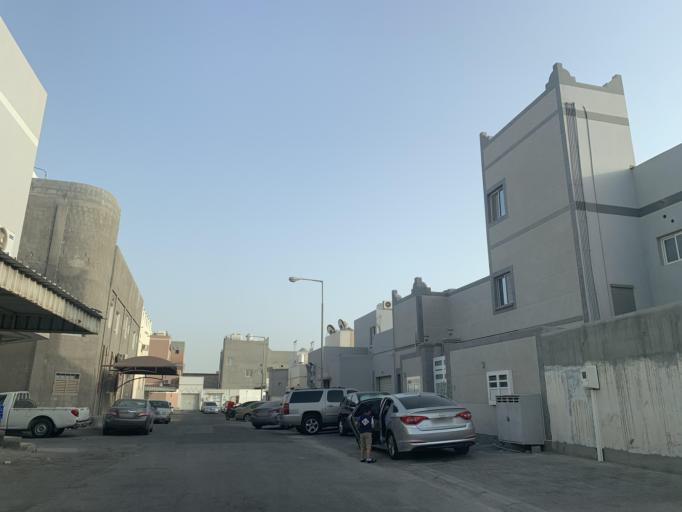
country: BH
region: Northern
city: Madinat `Isa
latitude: 26.1615
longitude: 50.5107
